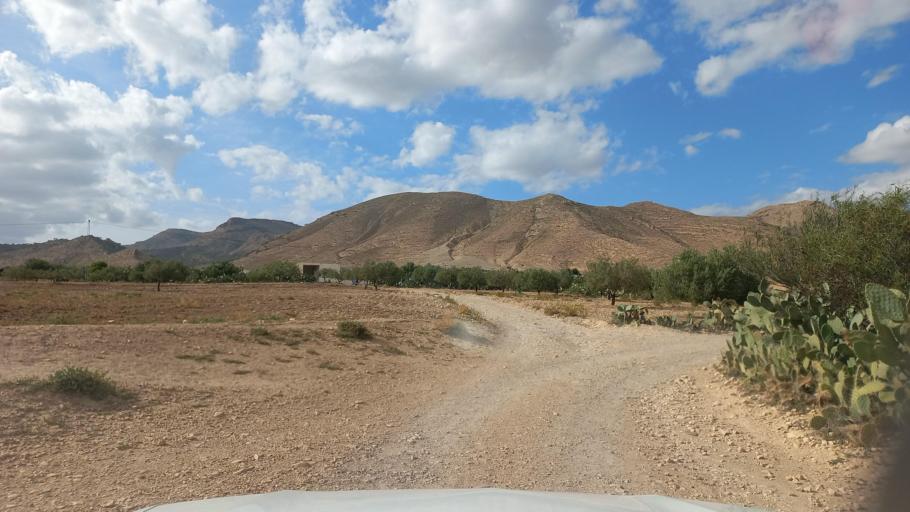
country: TN
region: Al Qasrayn
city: Sbiba
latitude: 35.4510
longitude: 9.0727
